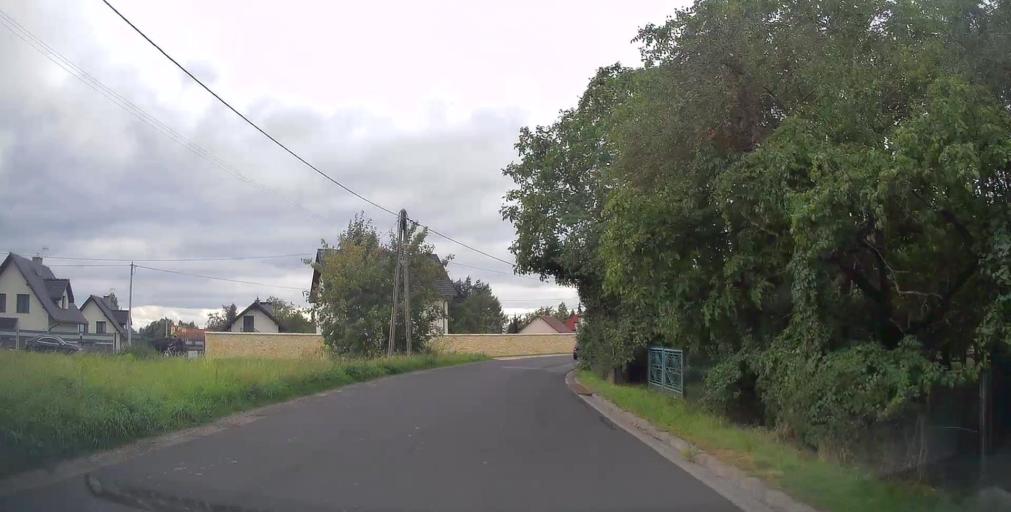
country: PL
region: Lesser Poland Voivodeship
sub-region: Powiat chrzanowski
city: Alwernia
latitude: 50.0709
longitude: 19.5463
